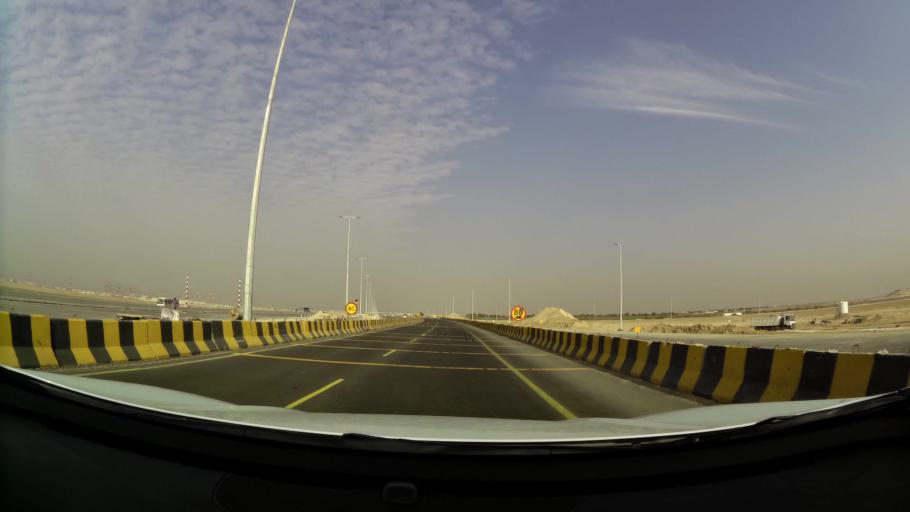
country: AE
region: Abu Dhabi
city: Abu Dhabi
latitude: 24.2798
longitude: 54.5296
